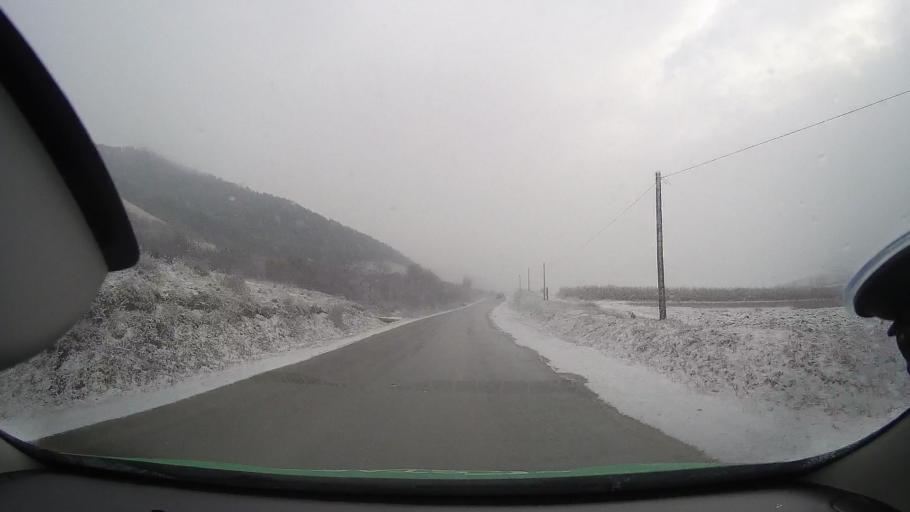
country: RO
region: Alba
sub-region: Comuna Lopadea Noua
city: Lopadea Noua
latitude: 46.3032
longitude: 23.8029
